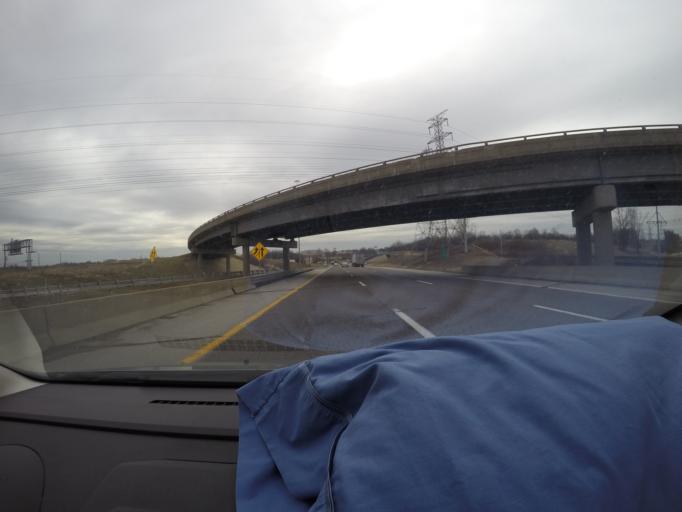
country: US
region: Missouri
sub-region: Saint Louis County
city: Saint Johns
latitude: 38.7283
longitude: -90.3310
